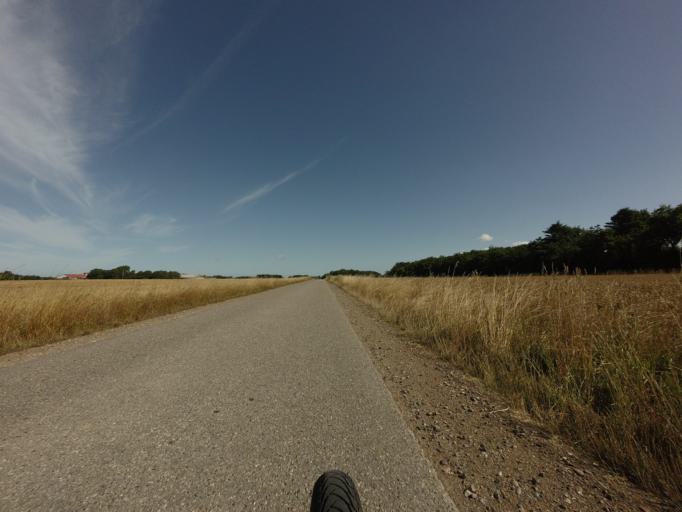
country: DK
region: North Denmark
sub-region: Hjorring Kommune
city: Vra
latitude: 57.3966
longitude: 9.9536
